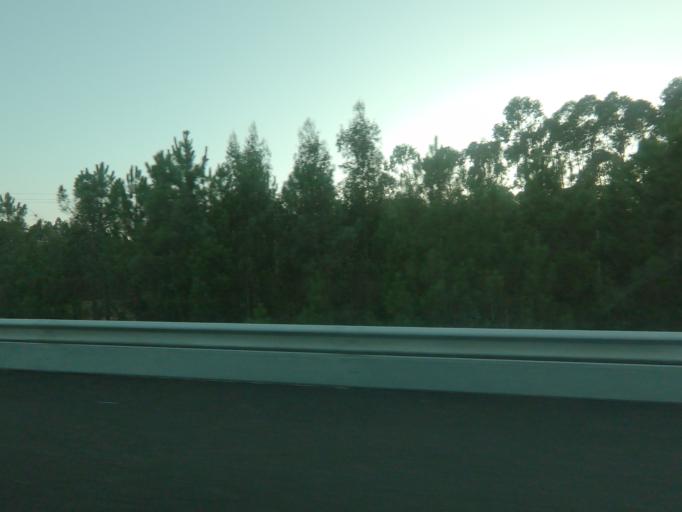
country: PT
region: Leiria
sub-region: Pombal
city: Pombal
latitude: 39.8961
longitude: -8.6902
